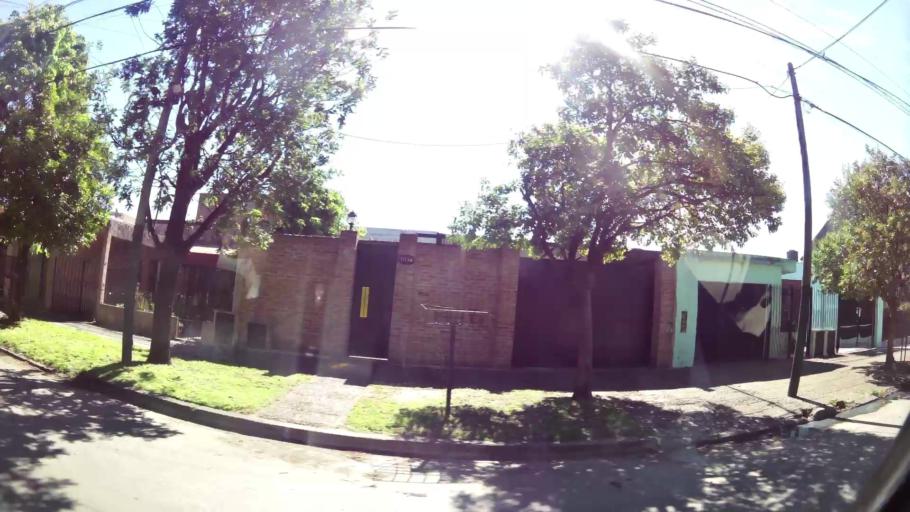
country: AR
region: Buenos Aires
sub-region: Partido de Lomas de Zamora
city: Lomas de Zamora
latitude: -34.7456
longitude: -58.4175
